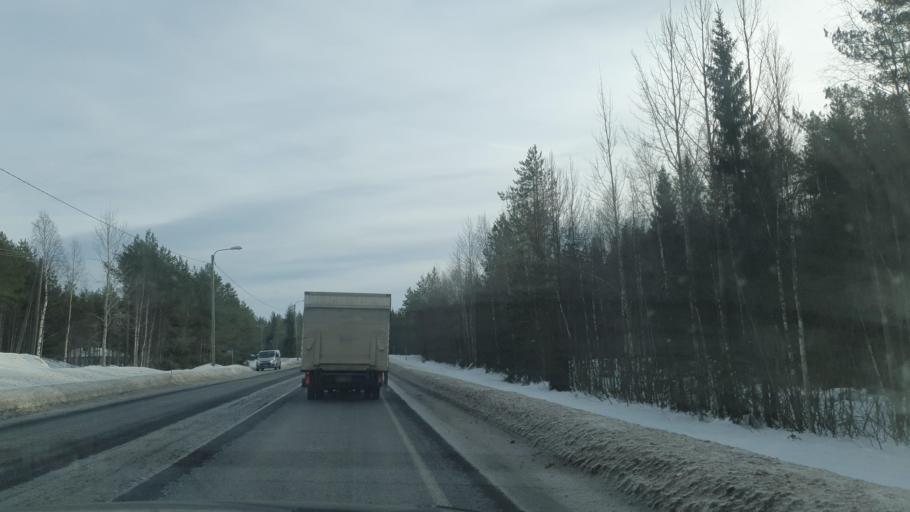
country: FI
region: Northern Ostrobothnia
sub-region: Oulu
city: Kempele
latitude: 64.9649
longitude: 25.6327
